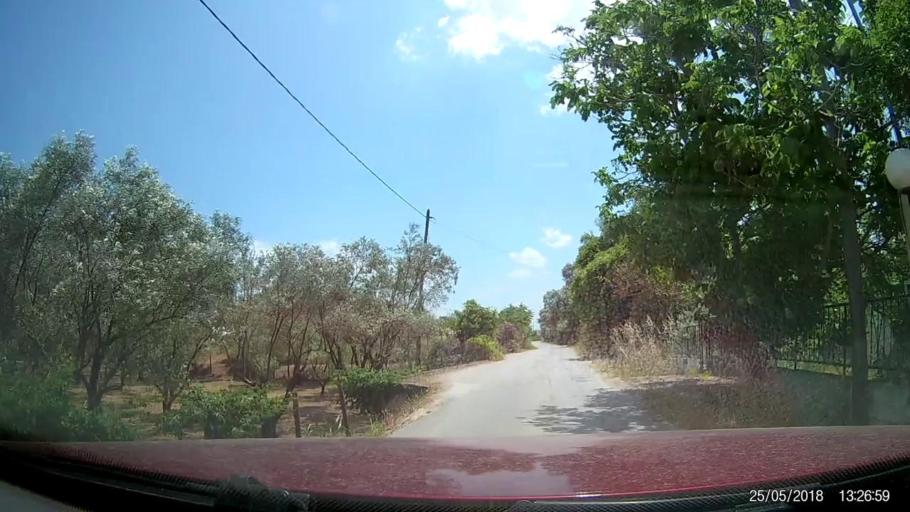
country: GR
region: Central Greece
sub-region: Nomos Evvoias
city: Mytikas
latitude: 38.4530
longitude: 23.6493
